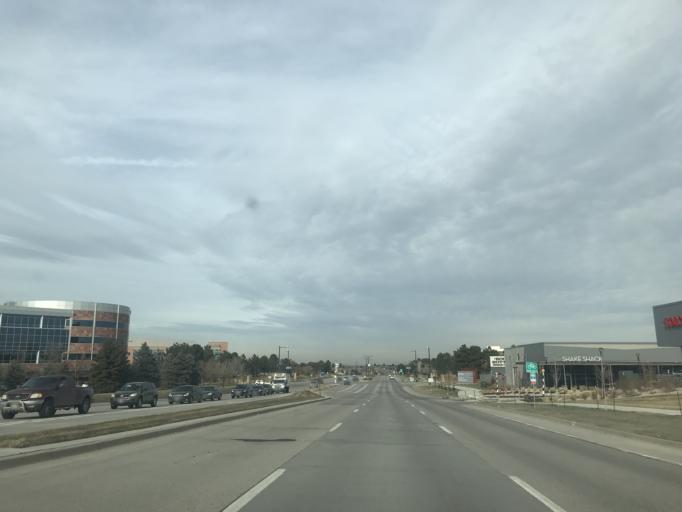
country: US
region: Colorado
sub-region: Douglas County
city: Highlands Ranch
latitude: 39.5537
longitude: -105.0081
